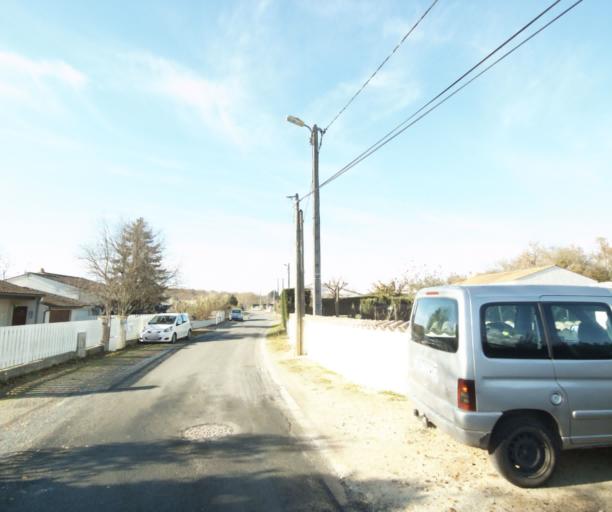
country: FR
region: Poitou-Charentes
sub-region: Departement de la Charente-Maritime
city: Ecoyeux
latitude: 45.7700
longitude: -0.4999
